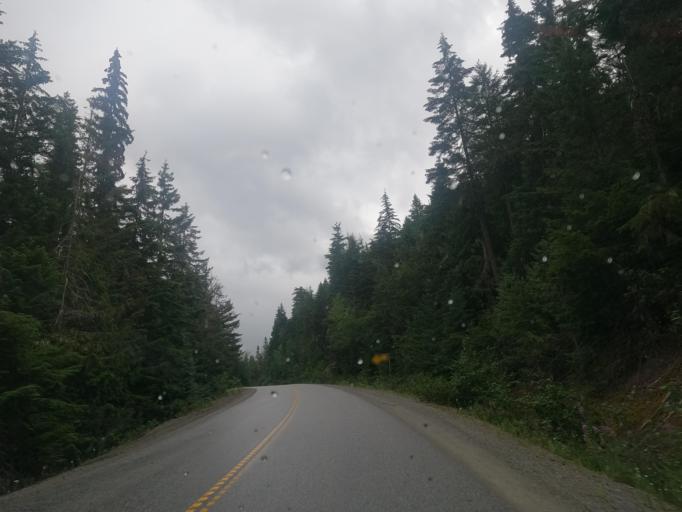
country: CA
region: British Columbia
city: Pemberton
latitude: 50.3300
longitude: -122.5523
